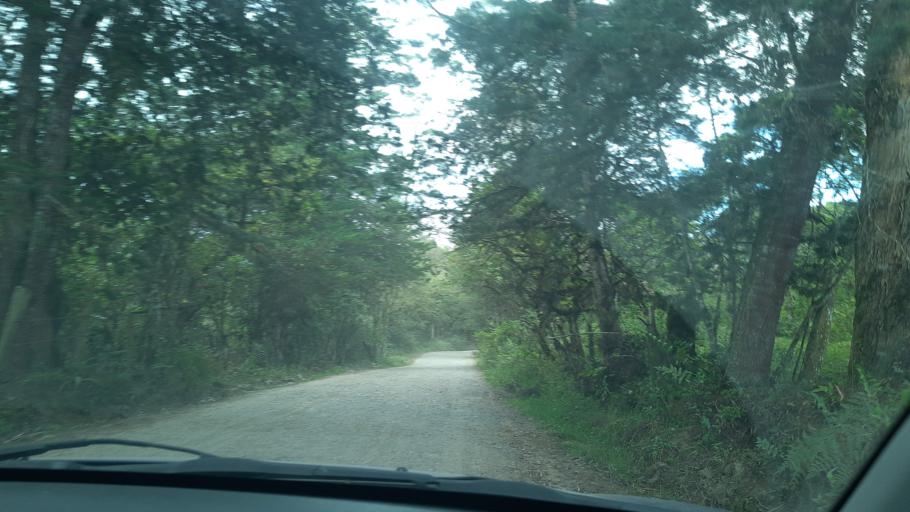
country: CO
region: Boyaca
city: Garagoa
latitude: 5.0882
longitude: -73.3412
